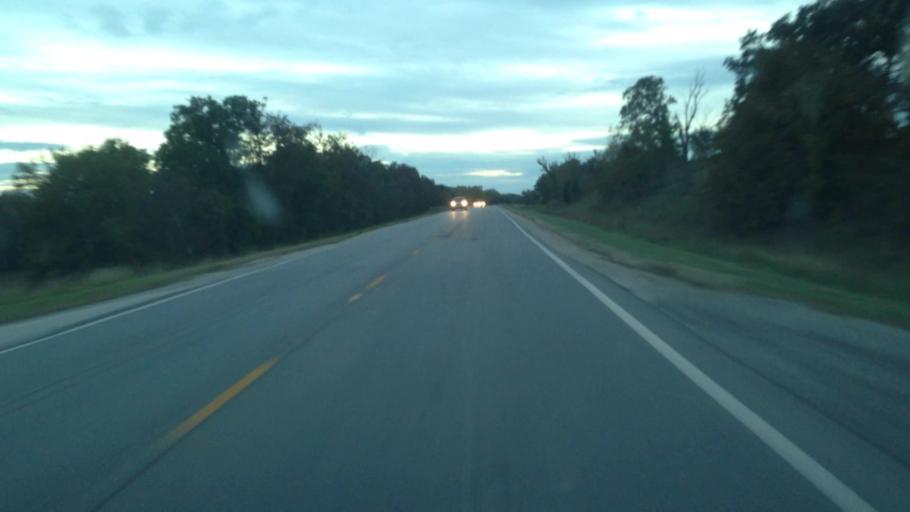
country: US
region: Kansas
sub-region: Anderson County
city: Garnett
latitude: 38.2082
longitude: -95.2490
